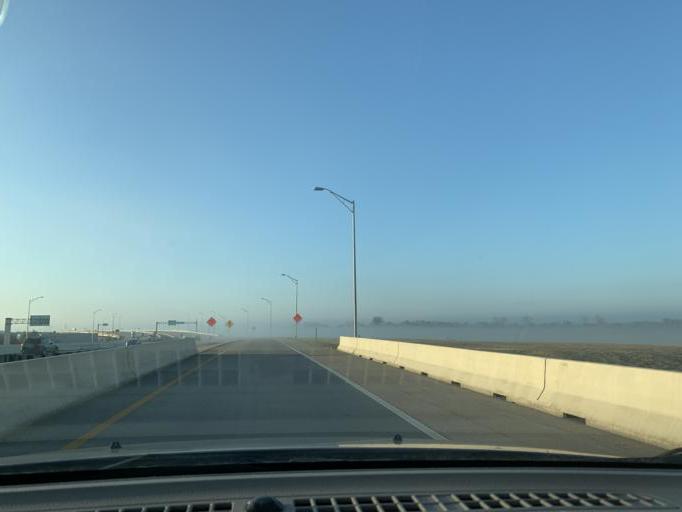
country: US
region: Texas
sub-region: Dallas County
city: Farmers Branch
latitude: 32.9462
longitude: -96.9284
